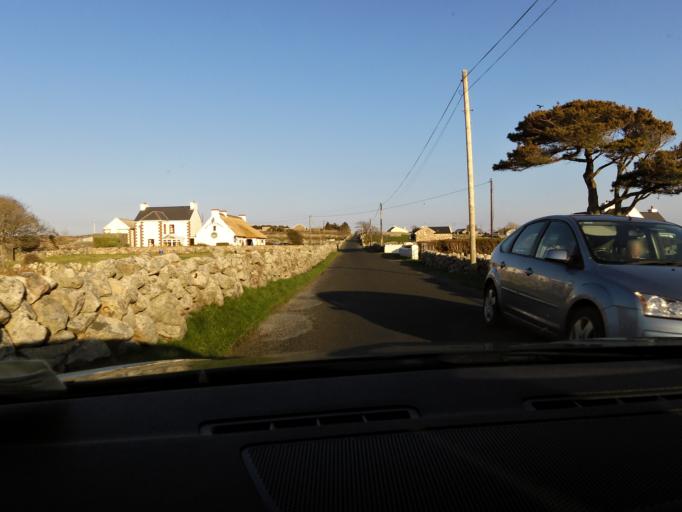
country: IE
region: Connaught
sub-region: County Galway
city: Oughterard
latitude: 53.2453
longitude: -9.5274
